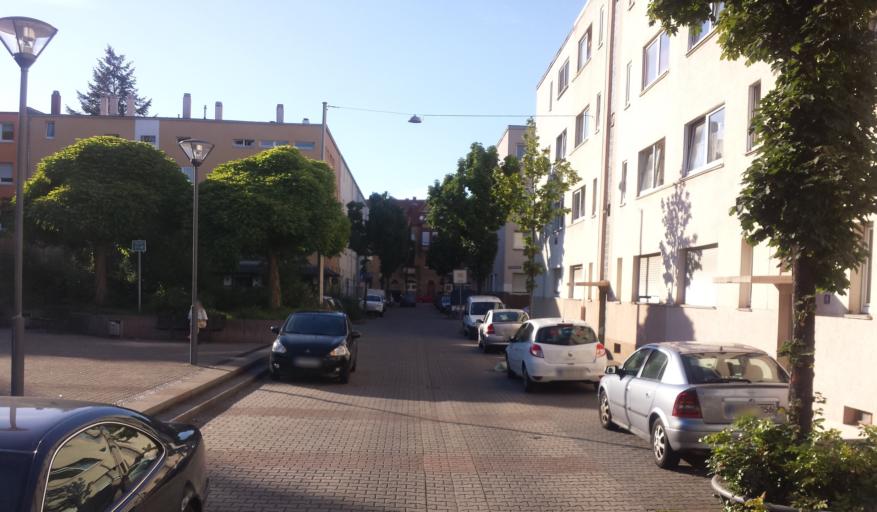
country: DE
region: Baden-Wuerttemberg
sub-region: Karlsruhe Region
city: Mannheim
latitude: 49.5272
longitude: 8.4804
